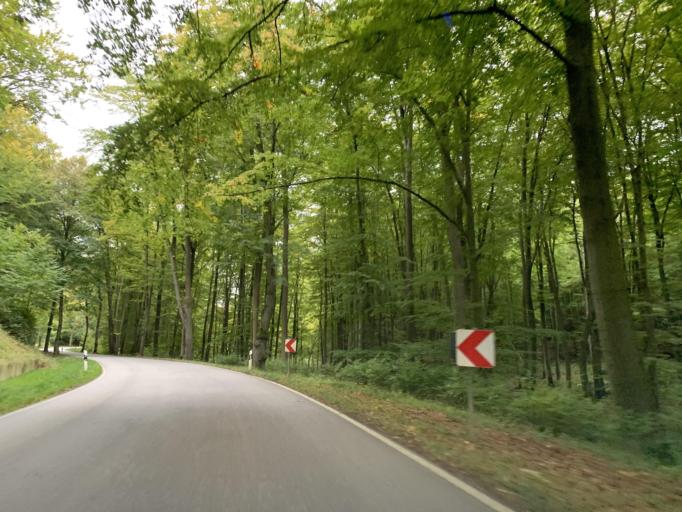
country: DE
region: Mecklenburg-Vorpommern
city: Burg Stargard
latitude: 53.4826
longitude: 13.2973
